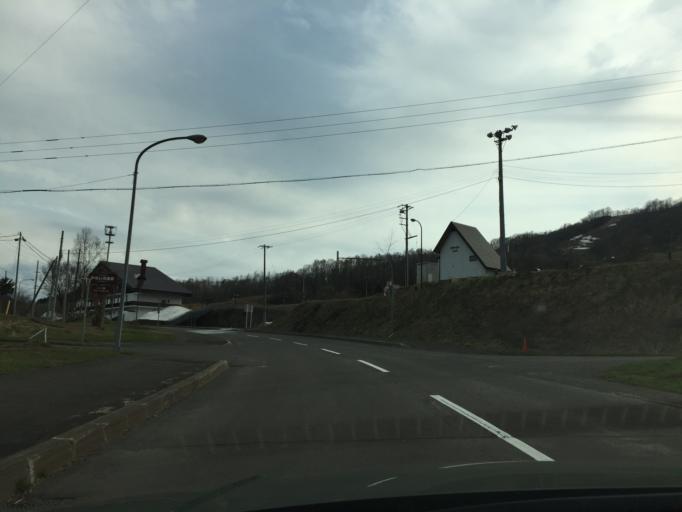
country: JP
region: Hokkaido
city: Utashinai
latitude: 43.5222
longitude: 142.0198
